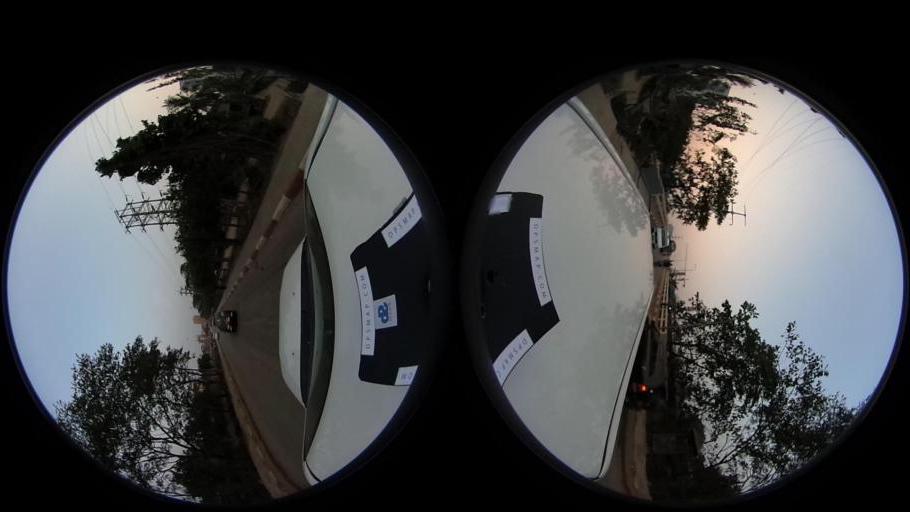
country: MM
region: Yangon
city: Yangon
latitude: 16.7845
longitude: 96.1798
